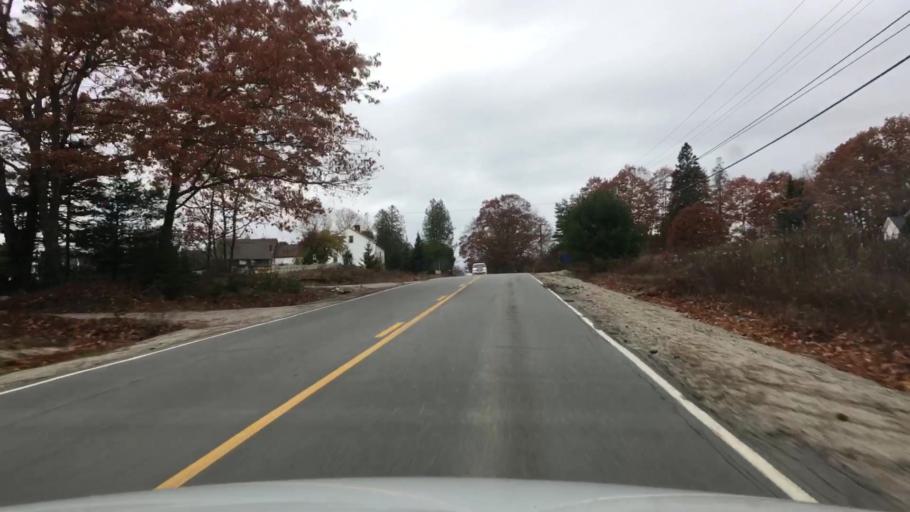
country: US
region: Maine
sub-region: Hancock County
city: Sedgwick
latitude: 44.3906
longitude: -68.5801
